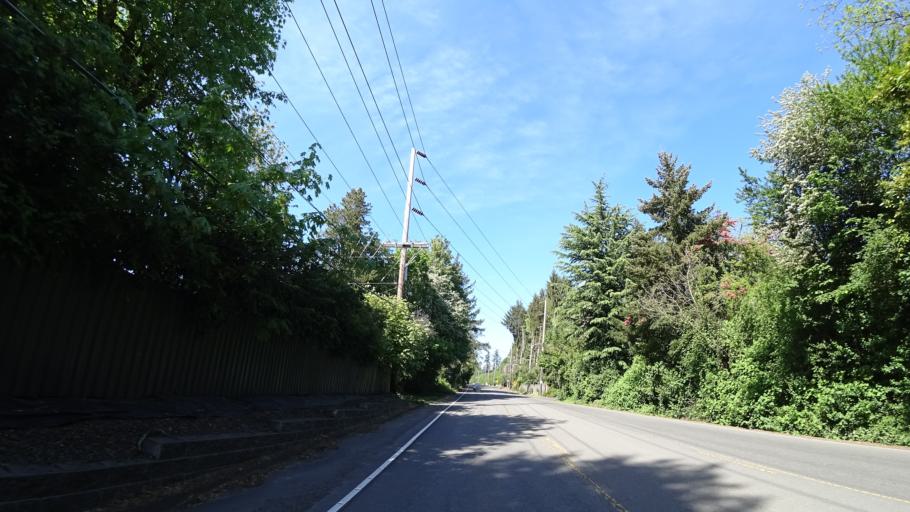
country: US
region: Oregon
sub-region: Washington County
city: Raleigh Hills
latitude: 45.4893
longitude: -122.7458
